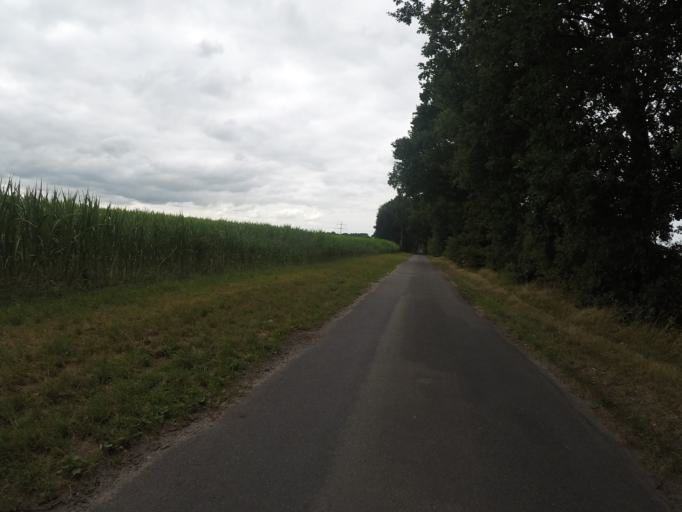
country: DE
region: Lower Saxony
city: Wingst
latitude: 53.6945
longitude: 9.0921
